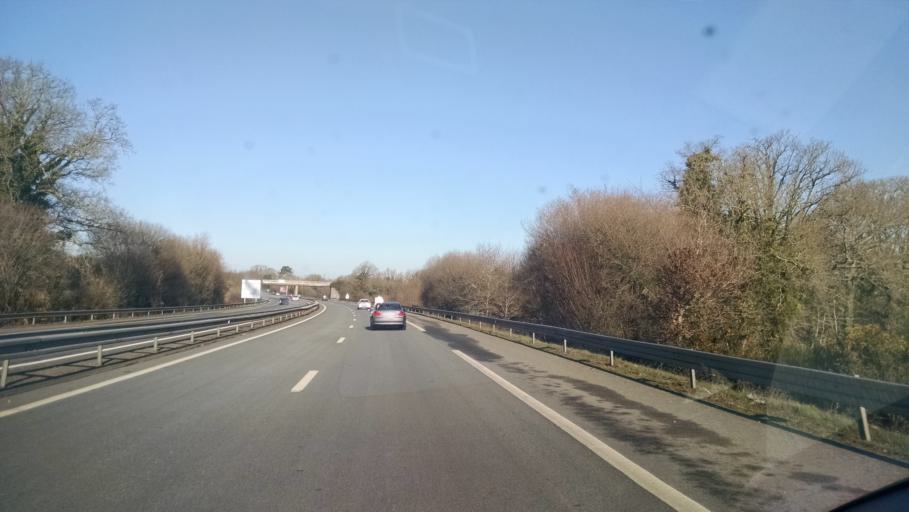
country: FR
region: Brittany
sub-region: Departement du Morbihan
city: Auray
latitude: 47.6775
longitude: -3.0180
